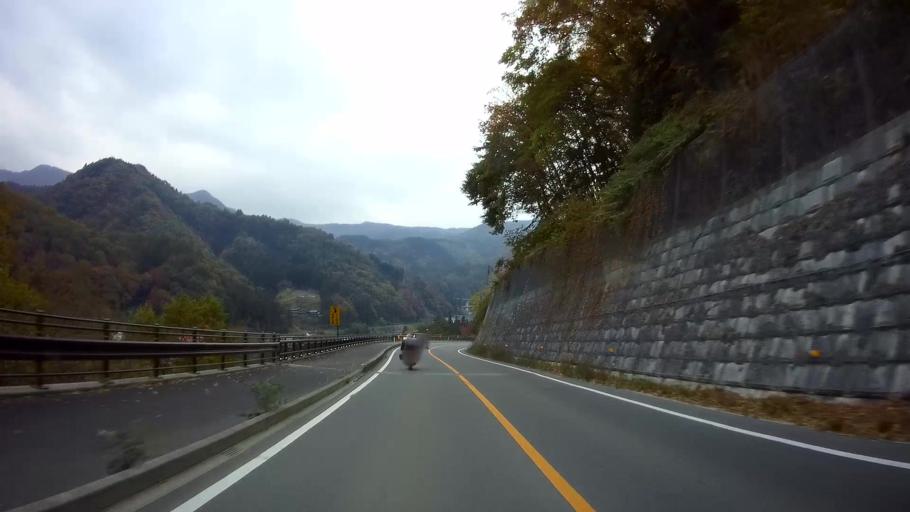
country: JP
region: Gunma
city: Nakanojomachi
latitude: 36.5648
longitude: 138.7298
